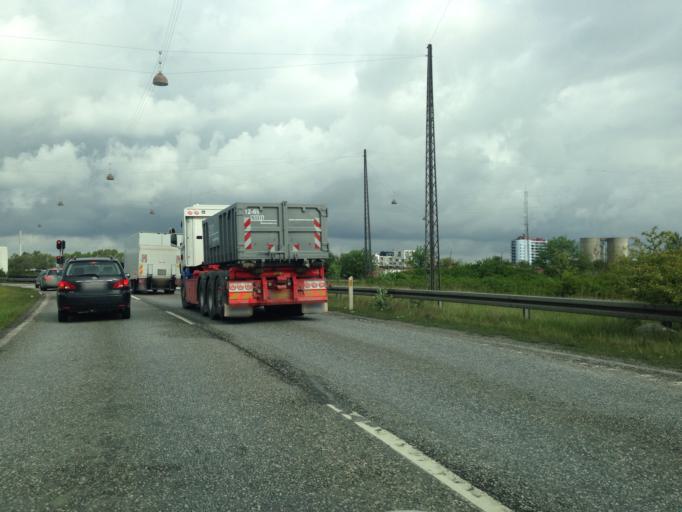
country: DK
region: Capital Region
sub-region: Kobenhavn
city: Copenhagen
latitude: 55.6404
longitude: 12.5544
